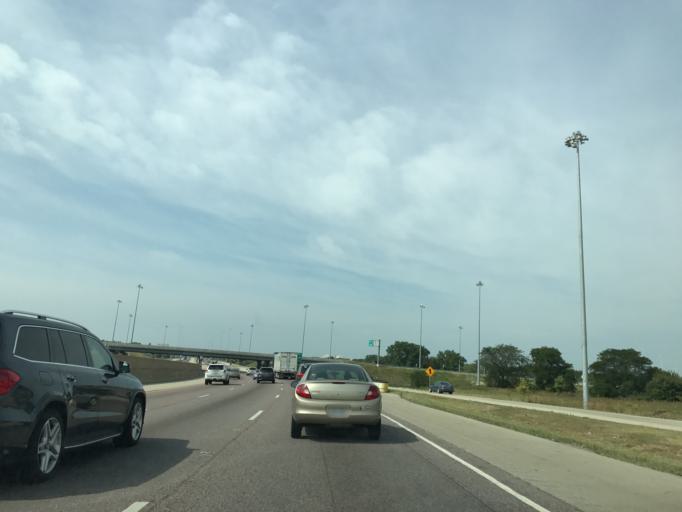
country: US
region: Illinois
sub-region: Cook County
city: Summit
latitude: 41.7953
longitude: -87.8192
